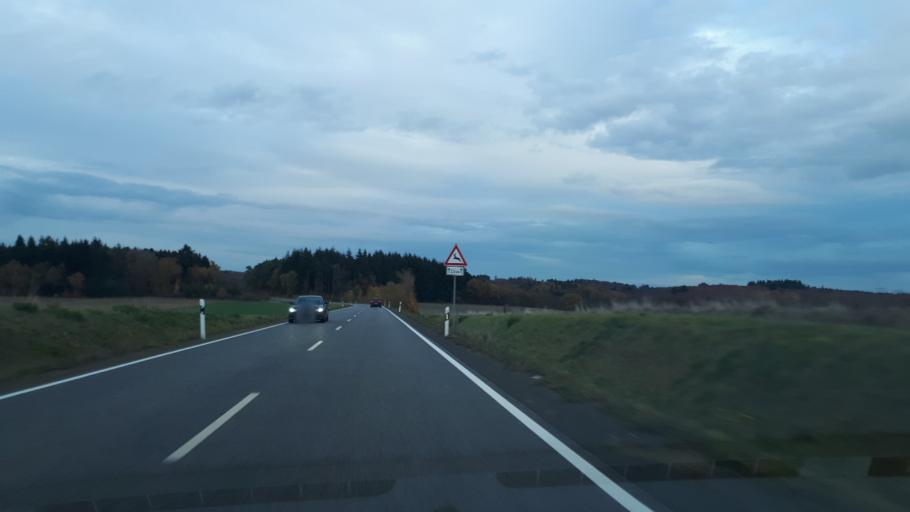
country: DE
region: Rheinland-Pfalz
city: Gillenbeuren
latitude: 50.1387
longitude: 7.0289
